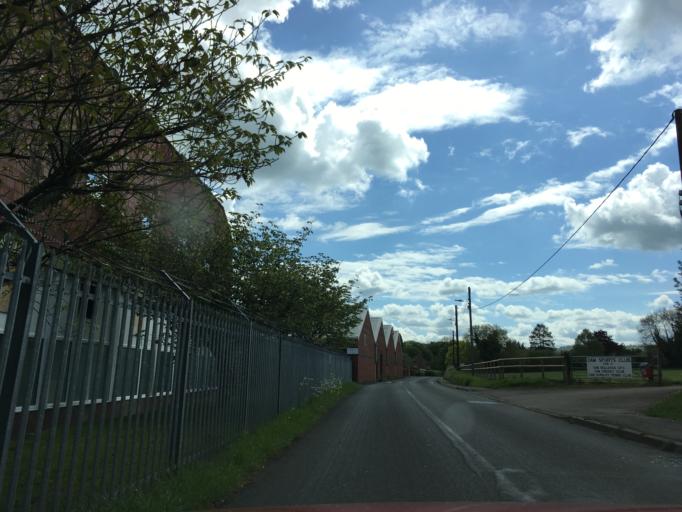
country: GB
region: England
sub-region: Gloucestershire
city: Dursley
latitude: 51.6977
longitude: -2.3589
